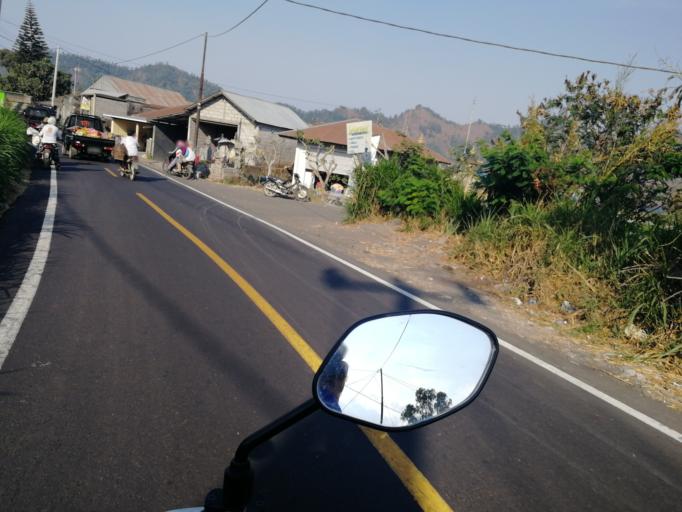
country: ID
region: Bali
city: Banjar Trunyan
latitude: -8.2414
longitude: 115.4043
